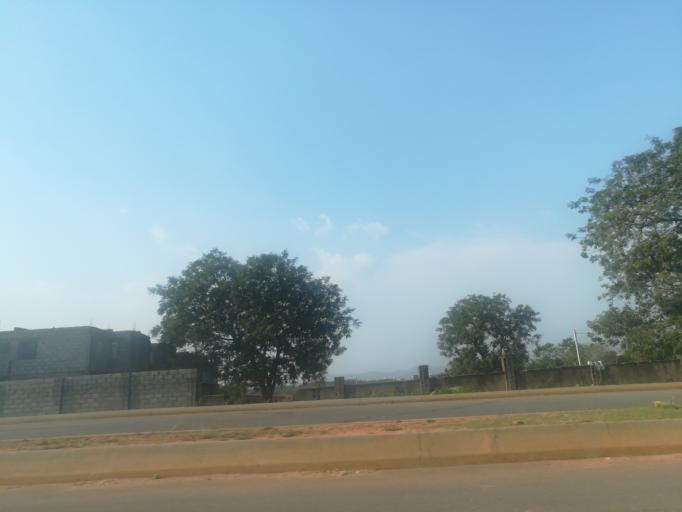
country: NG
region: Abuja Federal Capital Territory
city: Abuja
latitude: 9.0450
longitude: 7.4348
